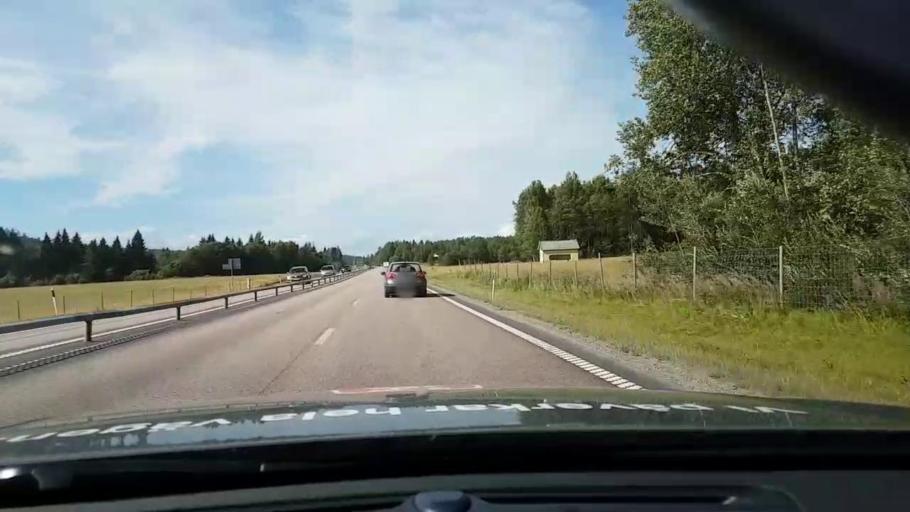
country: SE
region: Vaesternorrland
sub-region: OErnskoeldsviks Kommun
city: Ornskoldsvik
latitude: 63.2997
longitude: 18.8651
